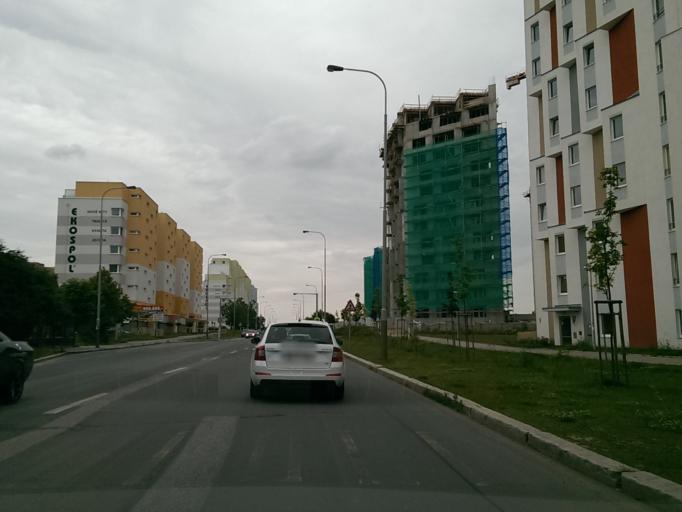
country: CZ
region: Central Bohemia
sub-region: Okres Praha-Zapad
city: Pruhonice
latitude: 50.0400
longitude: 14.5669
